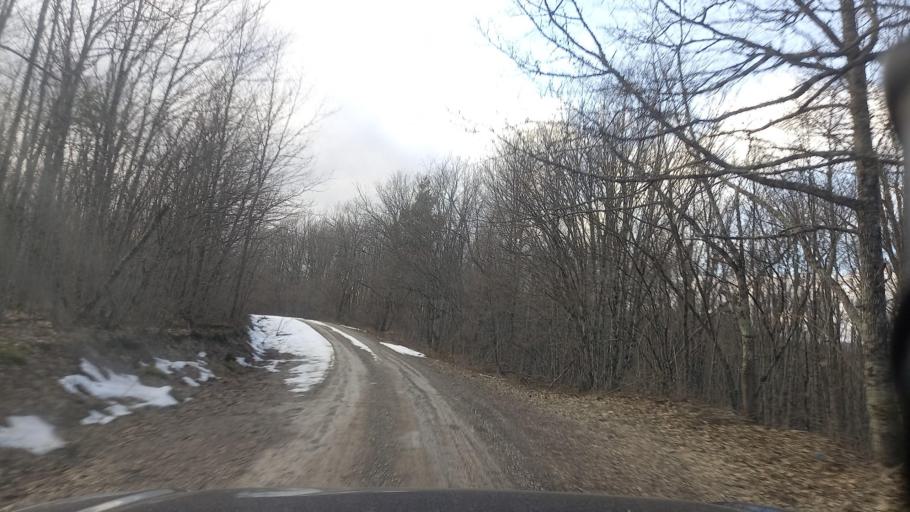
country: RU
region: Krasnodarskiy
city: Smolenskaya
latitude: 44.5755
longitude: 38.8044
